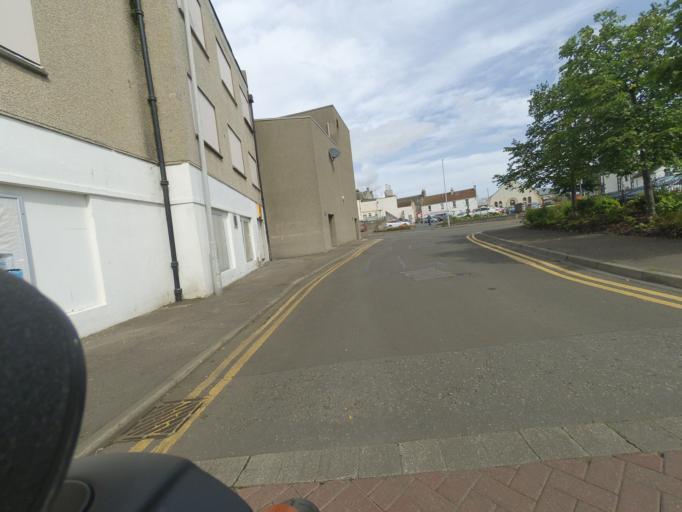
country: GB
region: Scotland
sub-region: Fife
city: Leven
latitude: 56.1942
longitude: -2.9972
